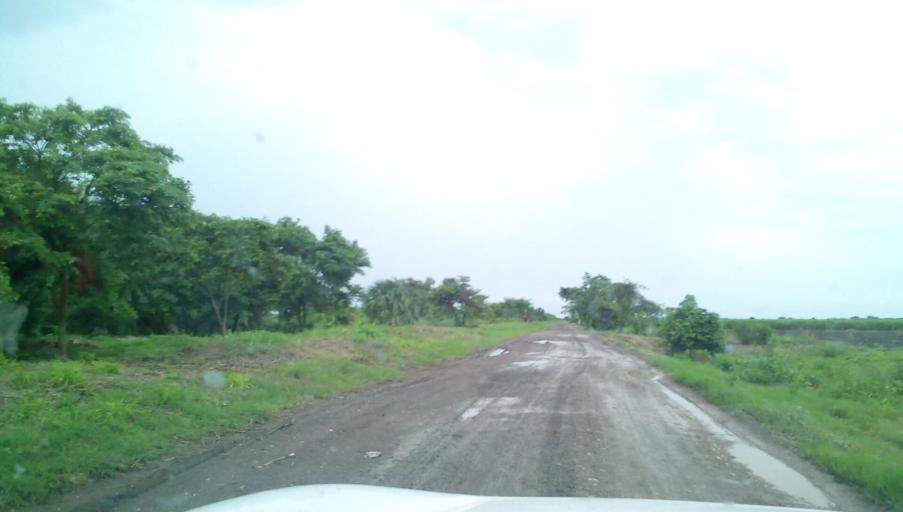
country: MX
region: Veracruz
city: Panuco
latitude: 21.8172
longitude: -98.1110
